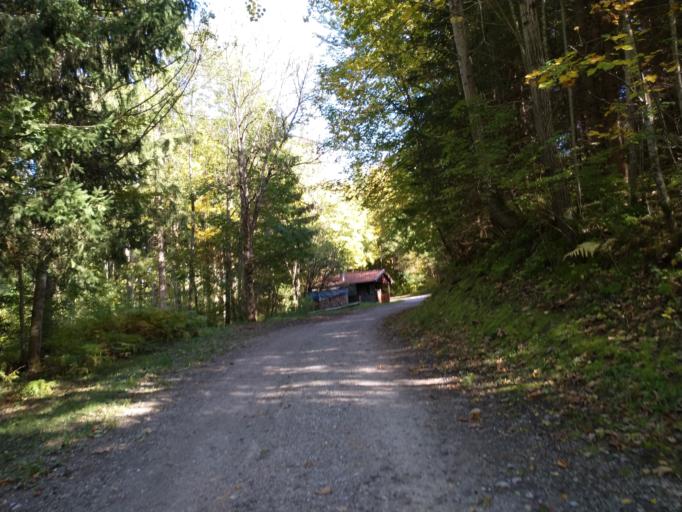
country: AT
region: Tyrol
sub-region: Politischer Bezirk Reutte
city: Vils
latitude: 47.5683
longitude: 10.6544
